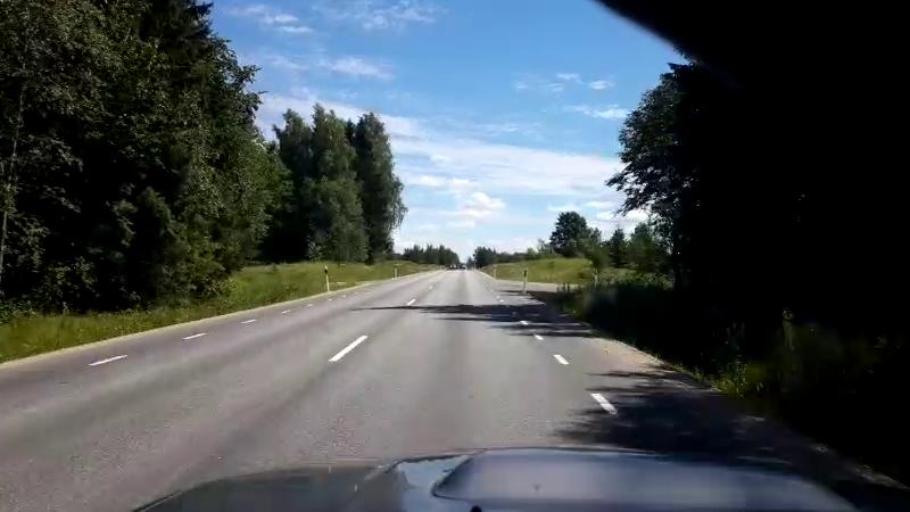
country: EE
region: Jogevamaa
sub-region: Jogeva linn
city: Jogeva
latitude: 58.7806
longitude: 26.3198
